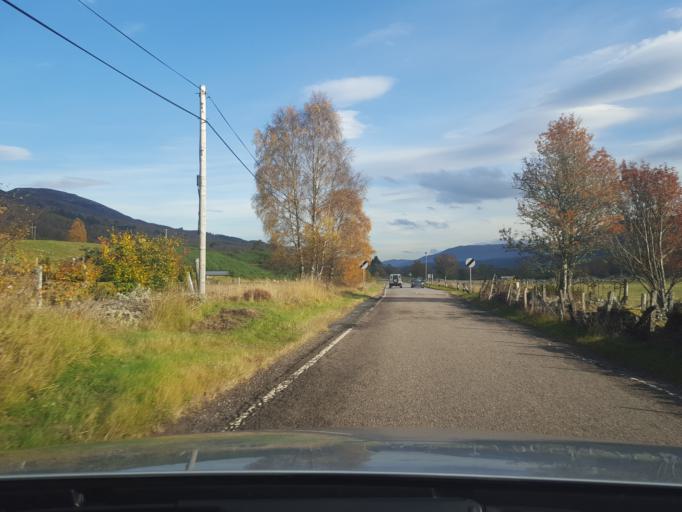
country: GB
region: Scotland
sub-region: Highland
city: Spean Bridge
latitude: 57.1857
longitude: -4.7874
